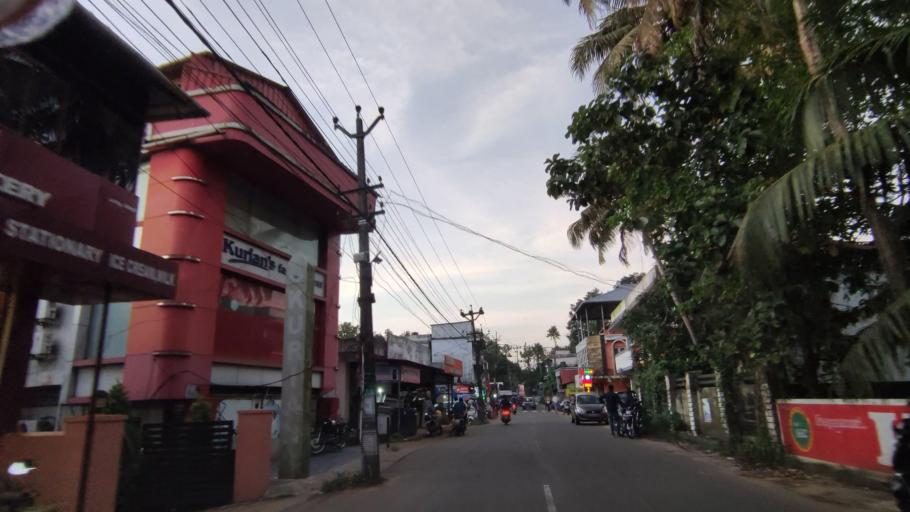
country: IN
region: Kerala
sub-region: Kottayam
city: Kottayam
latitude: 9.6793
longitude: 76.5057
